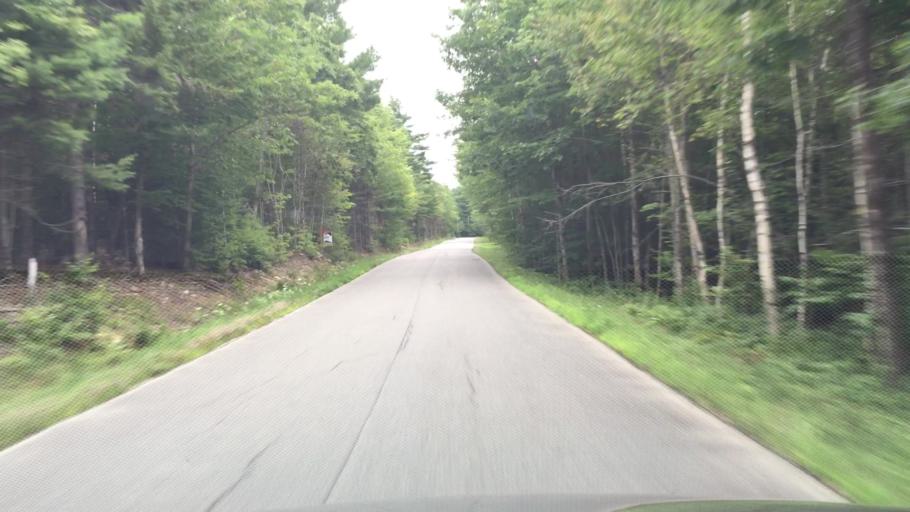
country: US
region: Maine
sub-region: Waldo County
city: Stockton Springs
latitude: 44.5207
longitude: -68.8798
